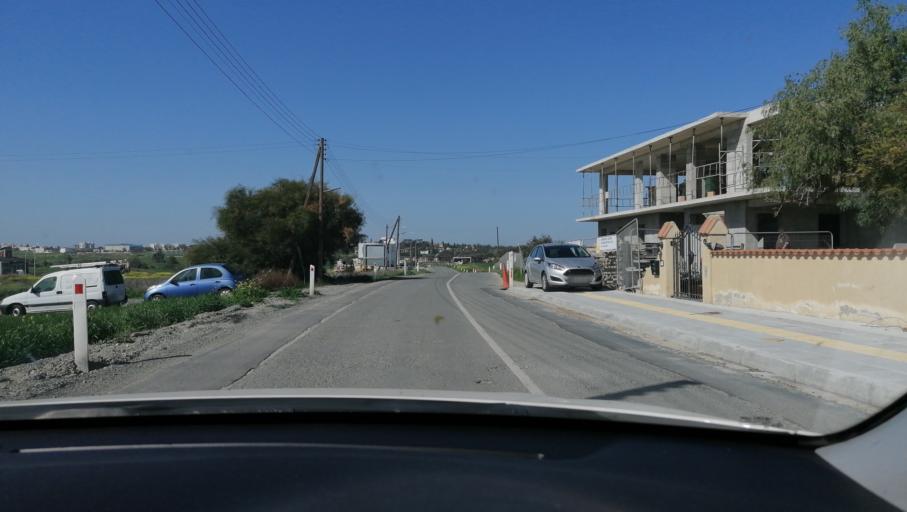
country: CY
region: Lefkosia
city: Geri
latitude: 35.1178
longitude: 33.4049
